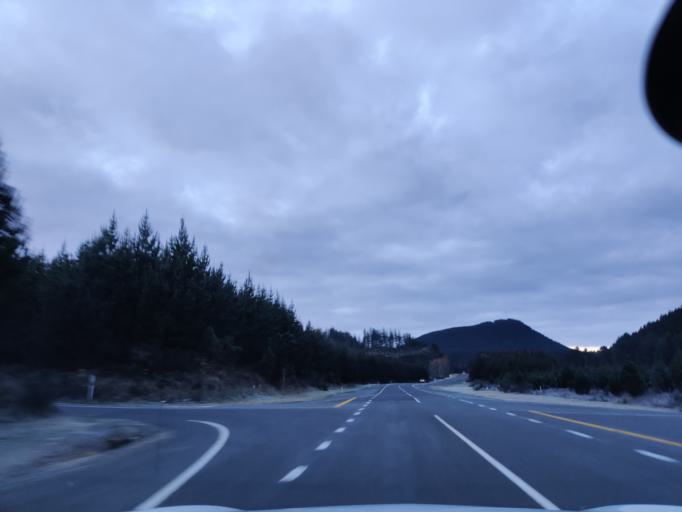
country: NZ
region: Waikato
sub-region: Taupo District
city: Taupo
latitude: -38.4243
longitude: 176.0564
